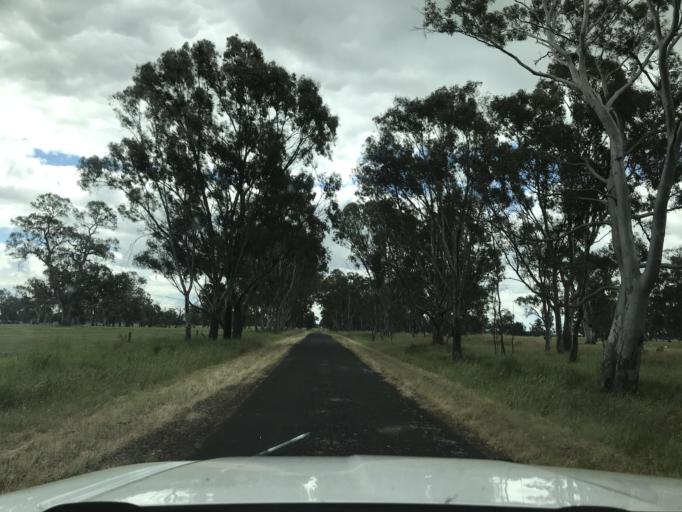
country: AU
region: South Australia
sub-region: Wattle Range
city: Penola
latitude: -37.0777
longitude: 141.1814
